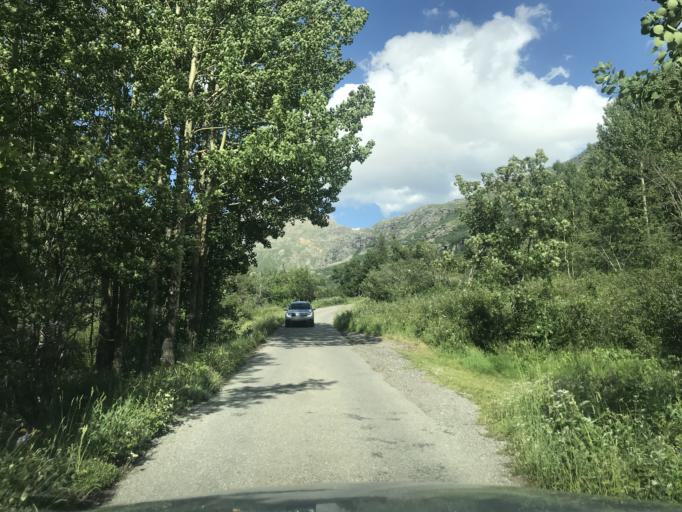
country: FR
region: Rhone-Alpes
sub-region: Departement de la Savoie
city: Val-d'Isere
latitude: 45.3731
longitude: 7.0655
